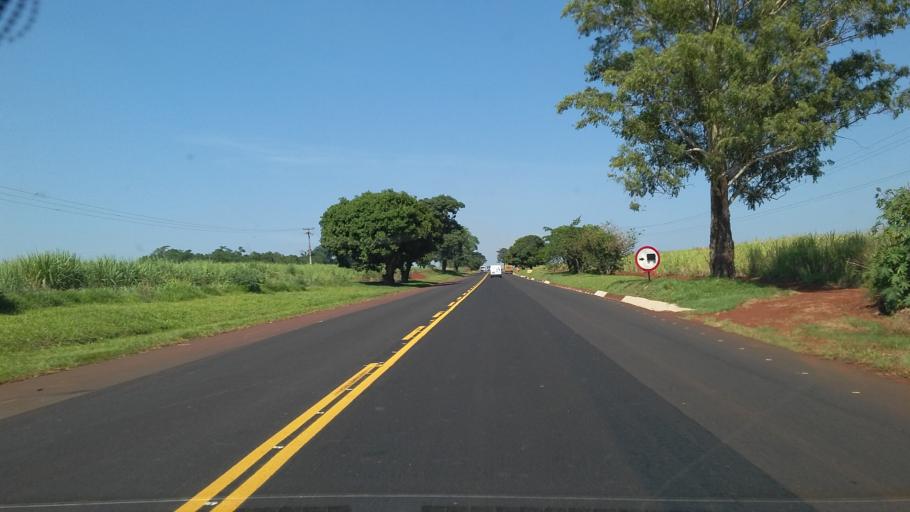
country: BR
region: Parana
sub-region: Bandeirantes
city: Bandeirantes
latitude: -23.1278
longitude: -50.4611
